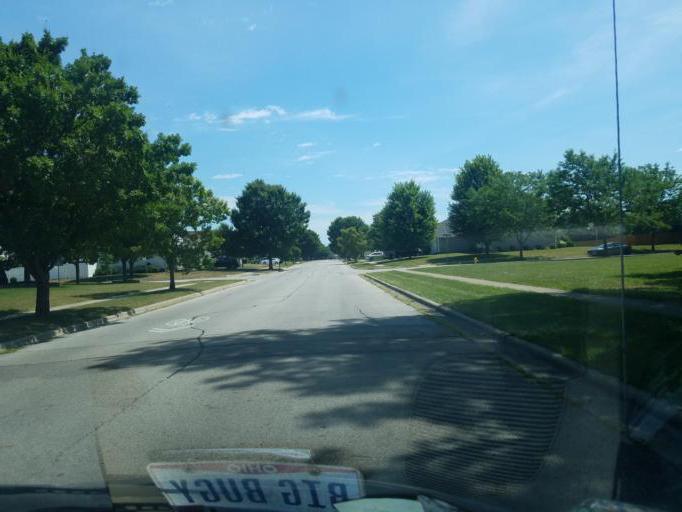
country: US
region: Ohio
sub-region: Franklin County
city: Grove City
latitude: 39.8701
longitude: -83.0948
